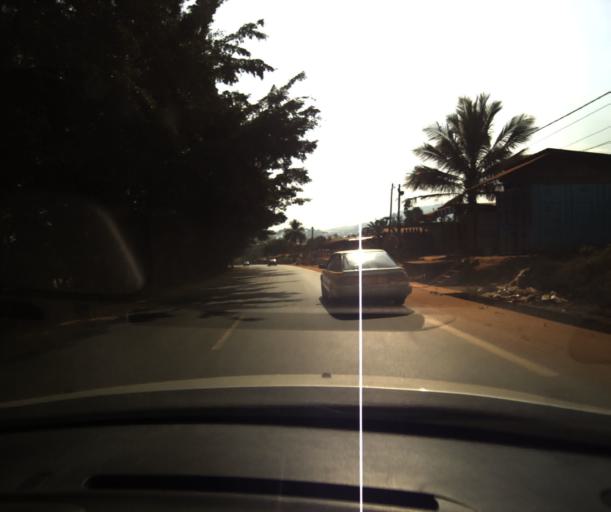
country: CM
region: Centre
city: Okoa
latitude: 3.9651
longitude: 11.5402
